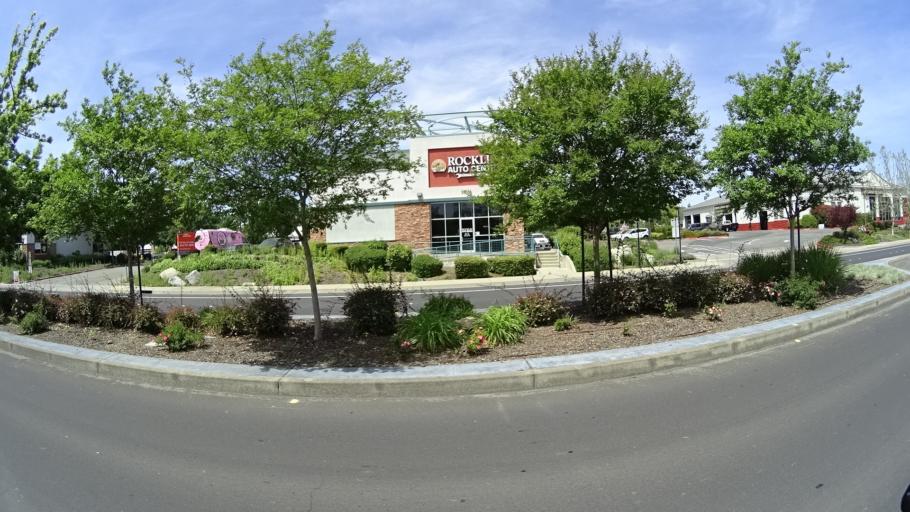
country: US
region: California
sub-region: Placer County
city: Rocklin
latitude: 38.7826
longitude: -121.2414
